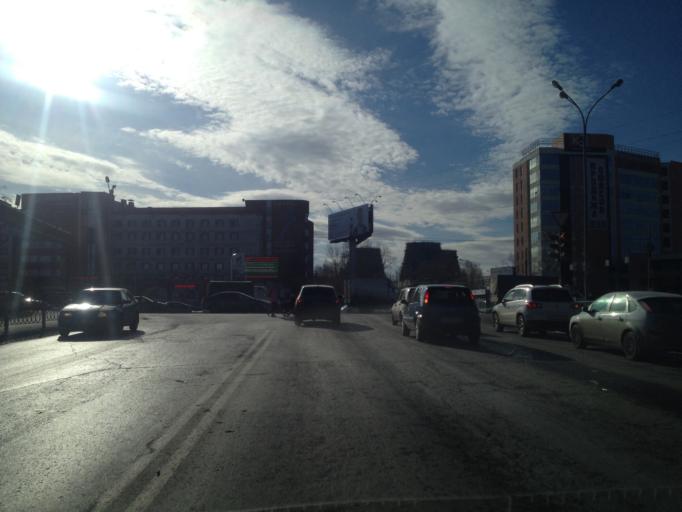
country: RU
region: Sverdlovsk
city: Yekaterinburg
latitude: 56.8467
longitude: 60.5617
